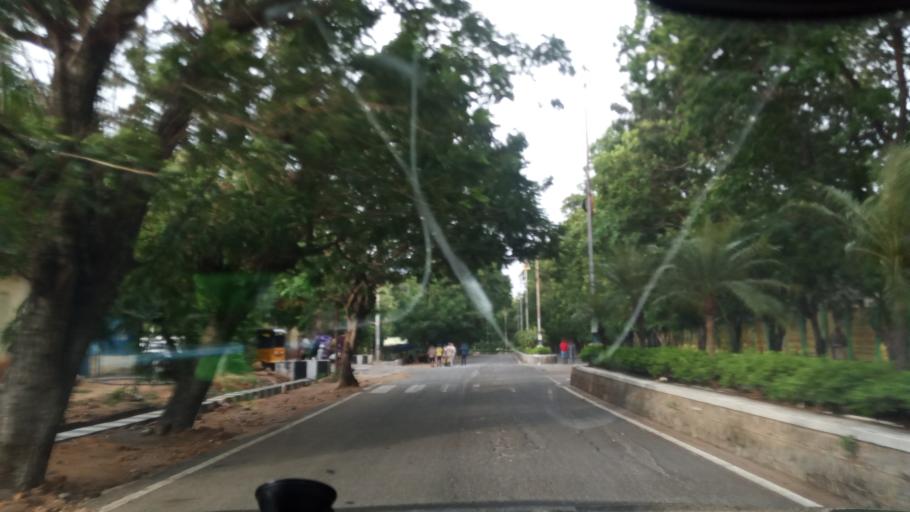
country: IN
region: Andhra Pradesh
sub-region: Chittoor
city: Akkarampalle
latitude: 13.6458
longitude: 79.4093
